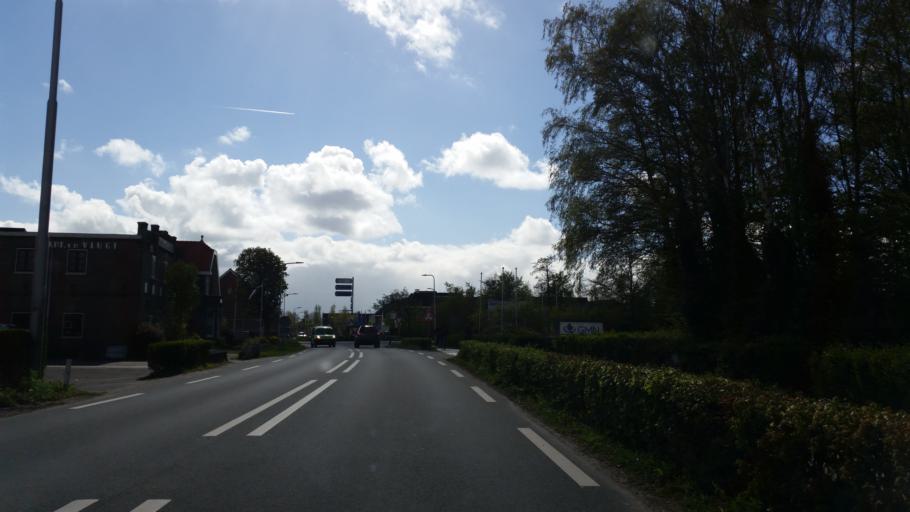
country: NL
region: South Holland
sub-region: Gemeente Teylingen
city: Voorhout
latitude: 52.2318
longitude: 4.4954
